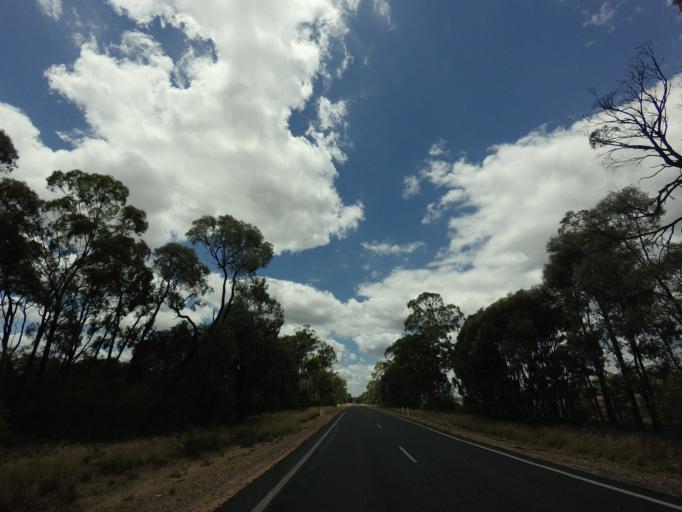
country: AU
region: Queensland
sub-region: Goondiwindi
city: Goondiwindi
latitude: -28.0160
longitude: 150.8645
